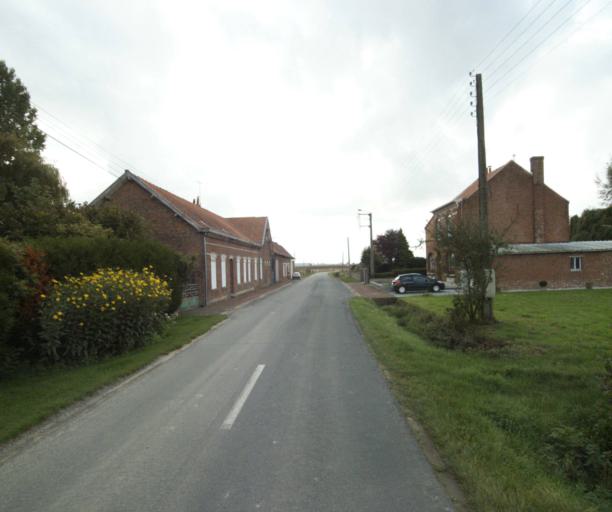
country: FR
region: Nord-Pas-de-Calais
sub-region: Departement du Nord
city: Herlies
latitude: 50.6037
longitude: 2.8538
